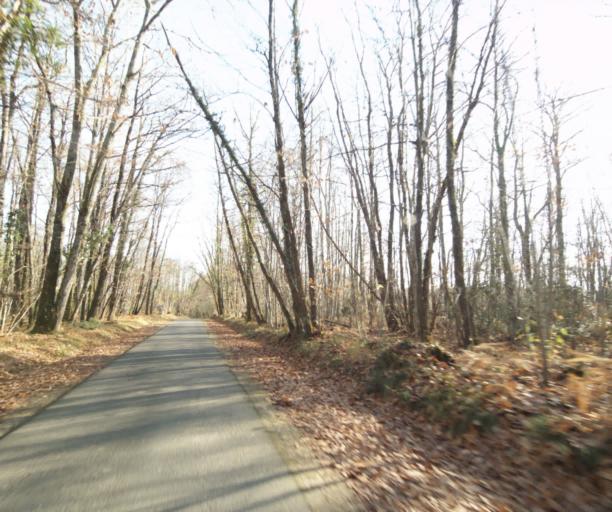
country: FR
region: Poitou-Charentes
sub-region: Departement de la Charente-Maritime
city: Burie
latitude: 45.7765
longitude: -0.4359
